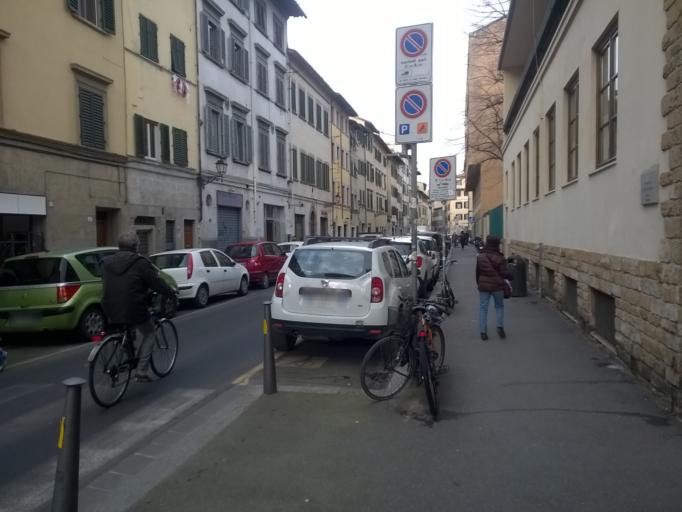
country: IT
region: Tuscany
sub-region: Province of Florence
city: Florence
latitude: 43.7704
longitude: 11.2640
